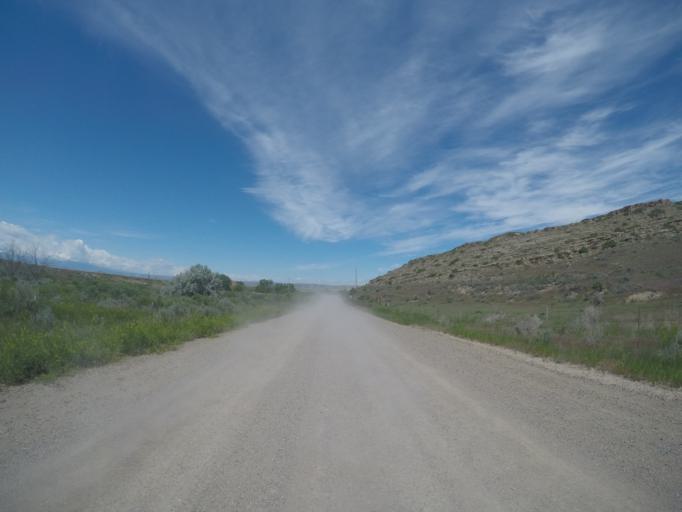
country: US
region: Montana
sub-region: Carbon County
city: Red Lodge
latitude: 45.2422
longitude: -108.8607
